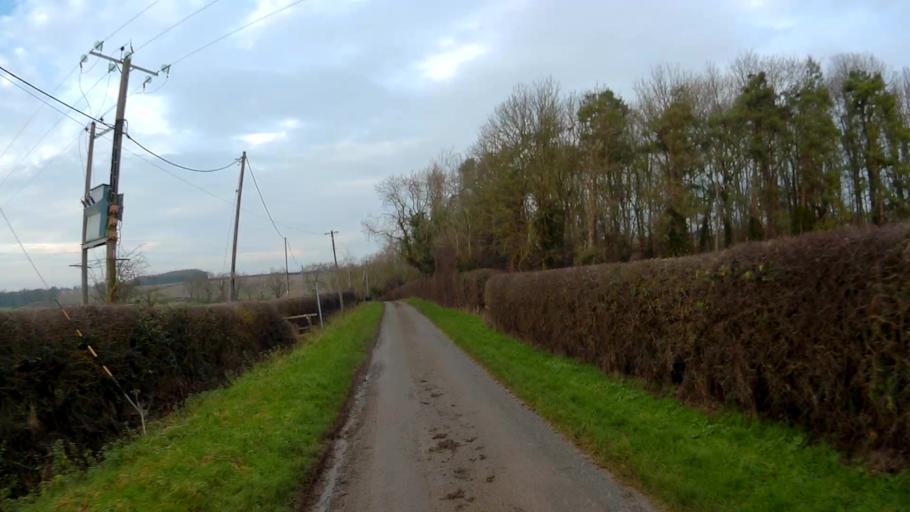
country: GB
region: England
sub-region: Lincolnshire
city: Bourne
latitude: 52.8252
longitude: -0.4598
